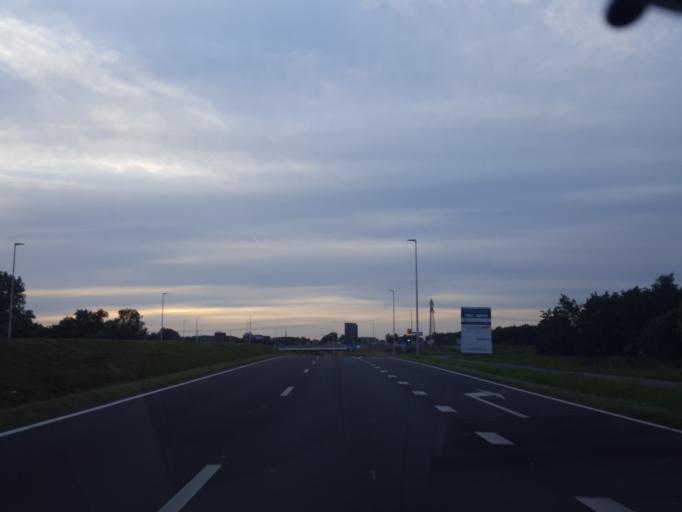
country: NL
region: Friesland
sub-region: Gemeente Leeuwarden
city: Huizum
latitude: 53.1779
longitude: 5.8231
